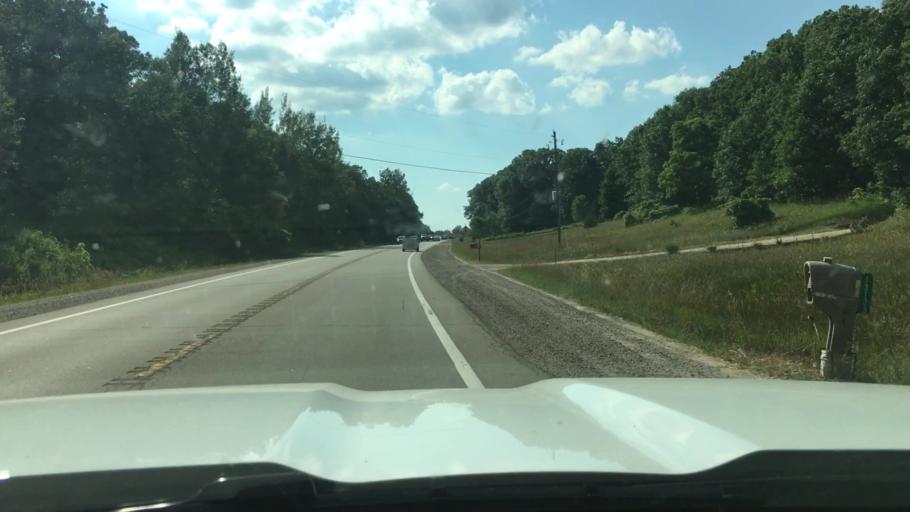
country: US
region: Michigan
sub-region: Montcalm County
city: Greenville
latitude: 43.1723
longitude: -85.3452
